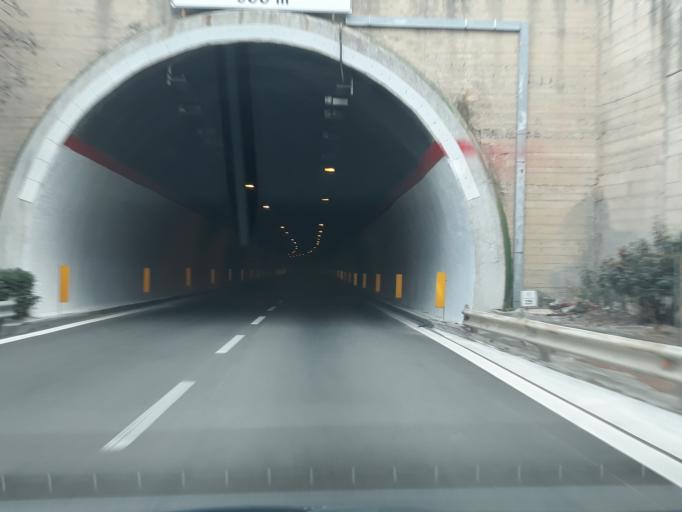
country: IT
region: Sicily
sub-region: Palermo
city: Termini Imerese
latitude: 37.9751
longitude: 13.6820
